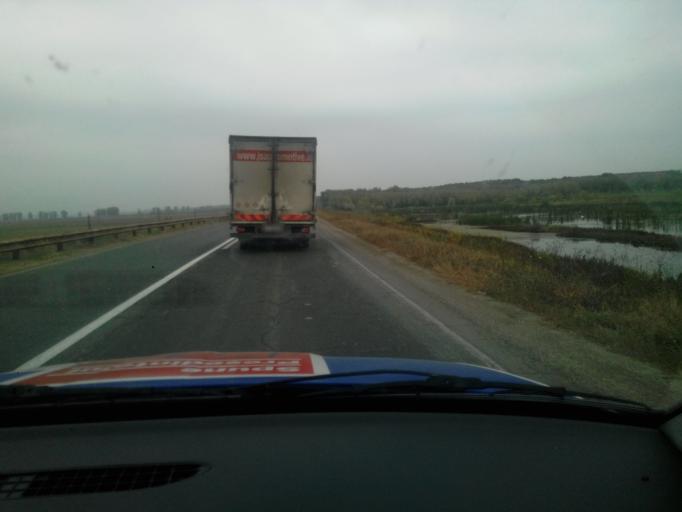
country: RO
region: Braila
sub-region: Municipiul Braila
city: Braila
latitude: 45.3152
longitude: 27.9855
